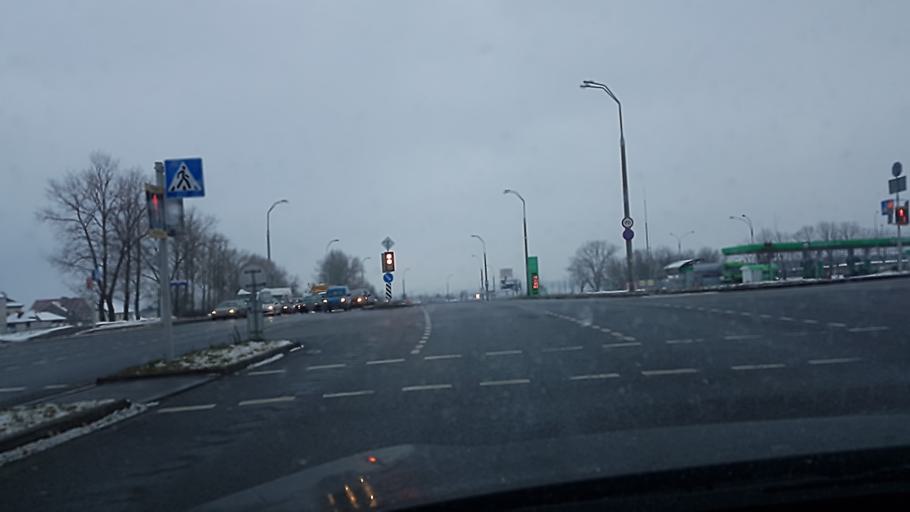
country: BY
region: Minsk
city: Bal'shavik
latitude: 53.9595
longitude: 27.5366
